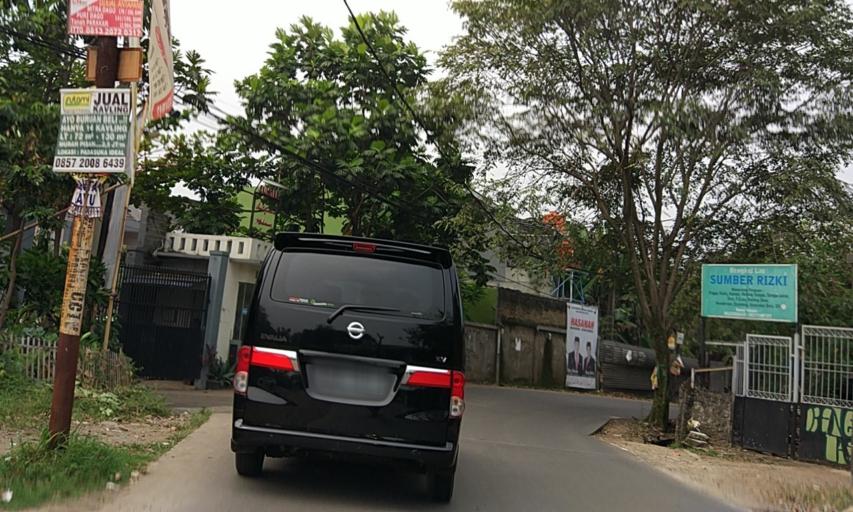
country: ID
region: West Java
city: Bandung
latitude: -6.9081
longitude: 107.6574
